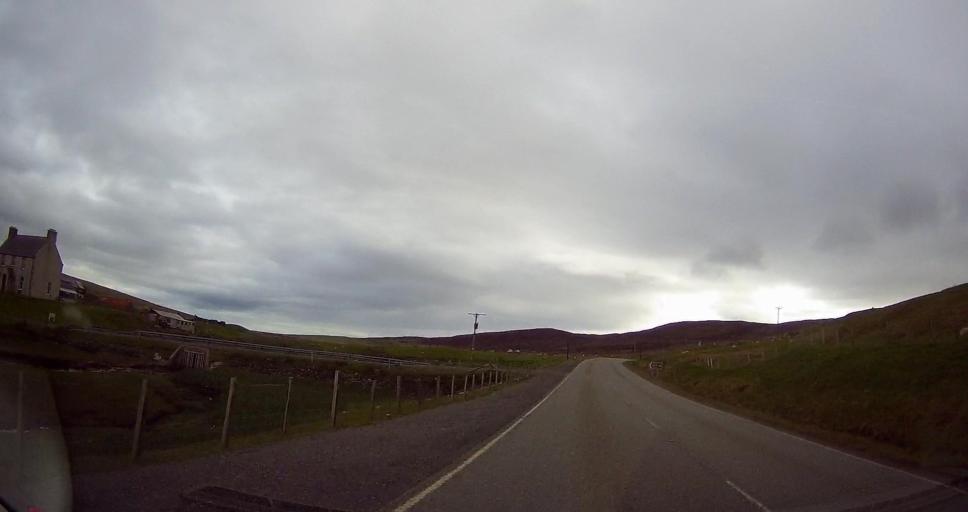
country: GB
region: Scotland
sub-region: Shetland Islands
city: Lerwick
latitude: 60.4103
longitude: -1.3284
